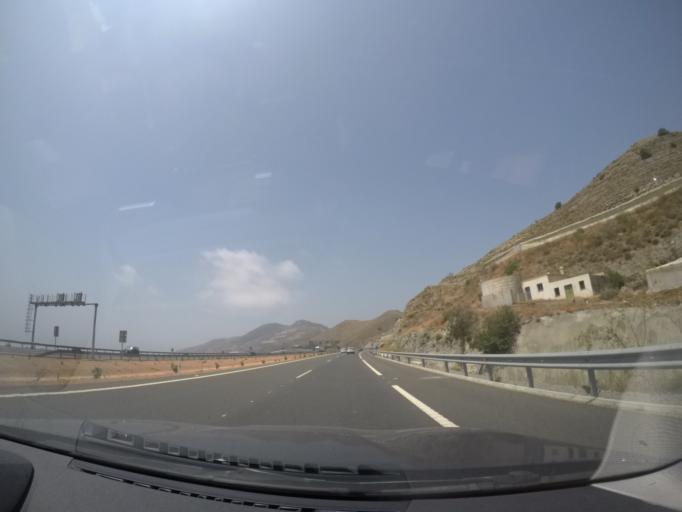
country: ES
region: Andalusia
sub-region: Provincia de Granada
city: Gualchos
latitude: 36.7166
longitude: -3.4462
